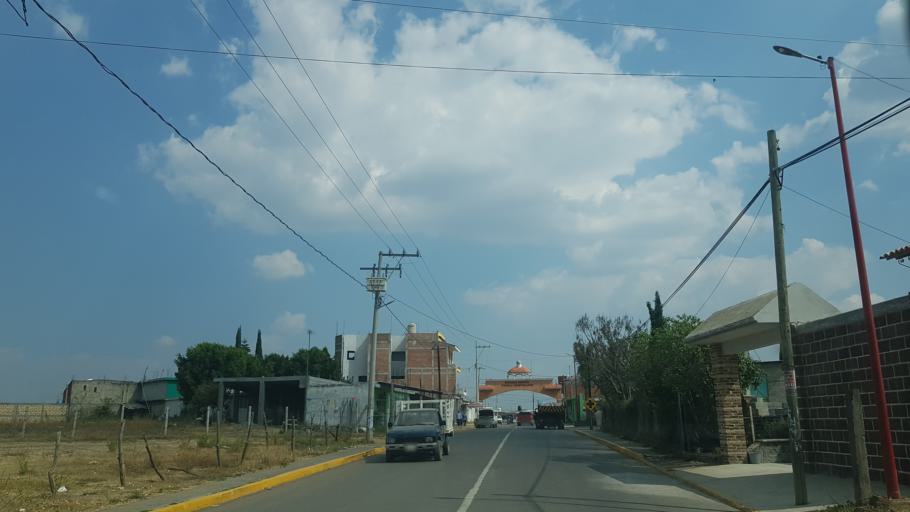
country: MX
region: Puebla
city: San Juan Amecac
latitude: 18.8280
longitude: -98.6566
